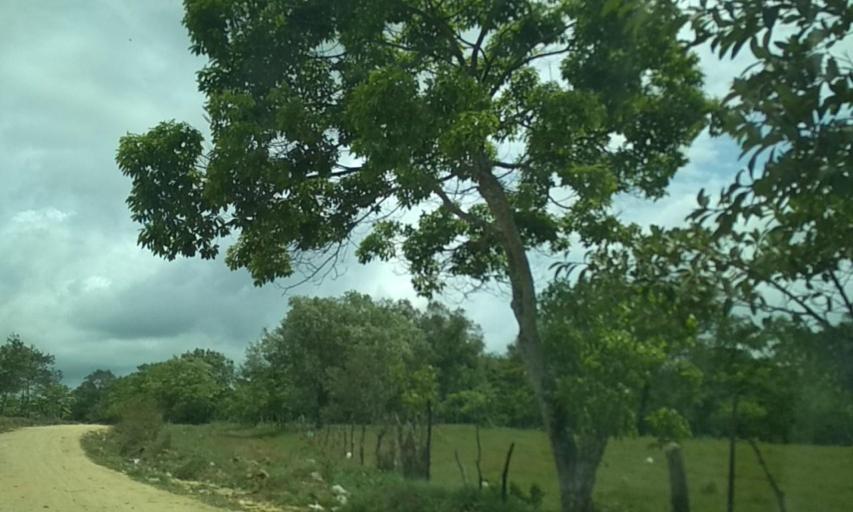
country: MX
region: Veracruz
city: Las Choapas
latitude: 17.9066
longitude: -94.1256
